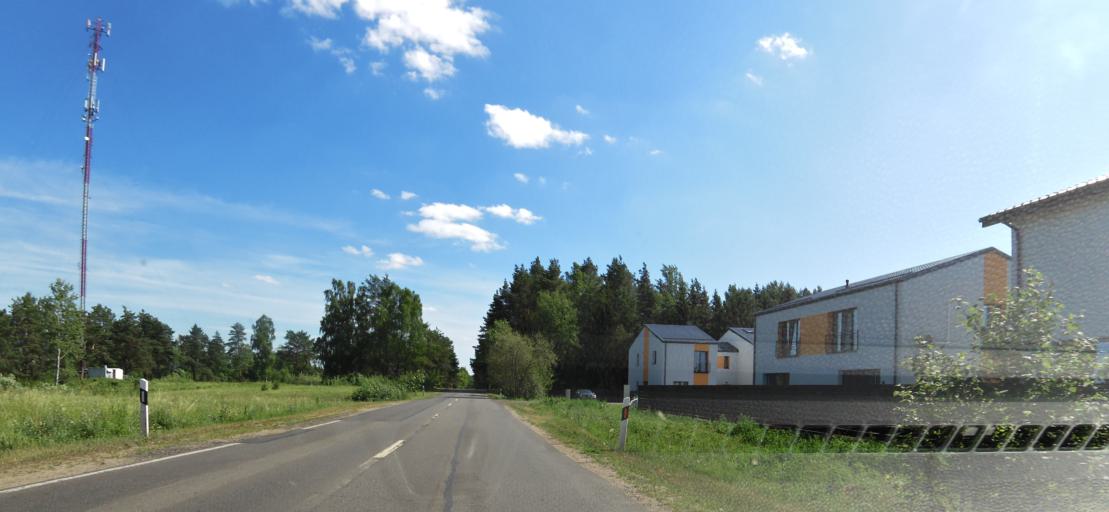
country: LT
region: Vilnius County
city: Rasos
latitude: 54.7984
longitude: 25.3490
